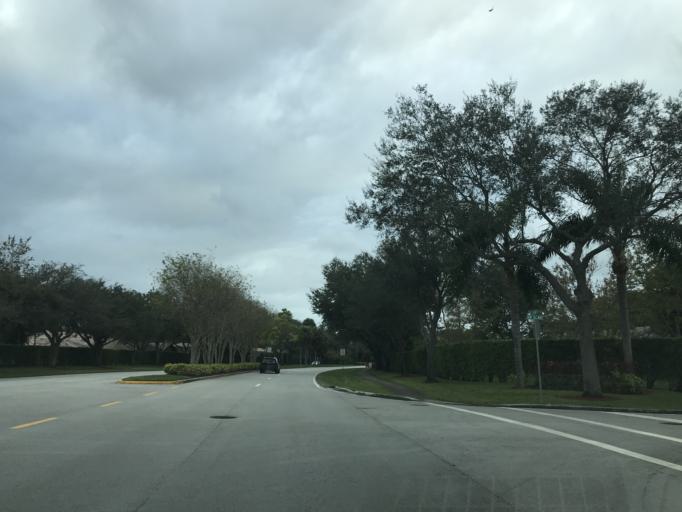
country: US
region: Florida
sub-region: Broward County
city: Parkland
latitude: 26.2989
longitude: -80.2419
